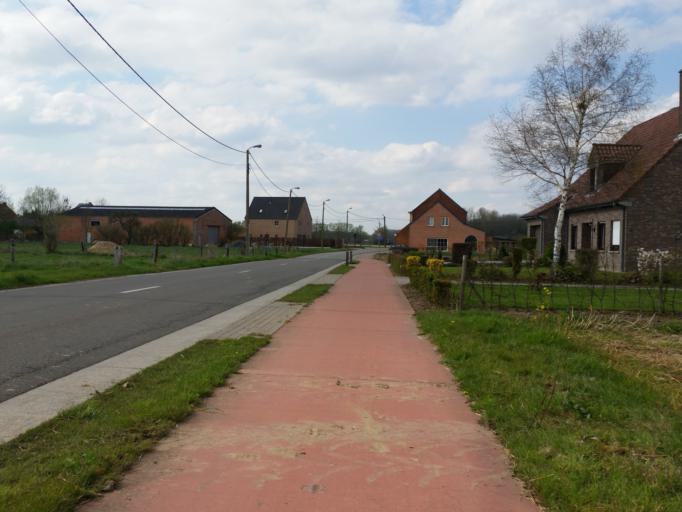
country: BE
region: Flanders
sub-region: Provincie Vlaams-Brabant
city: Kampenhout
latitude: 50.9409
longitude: 4.5349
